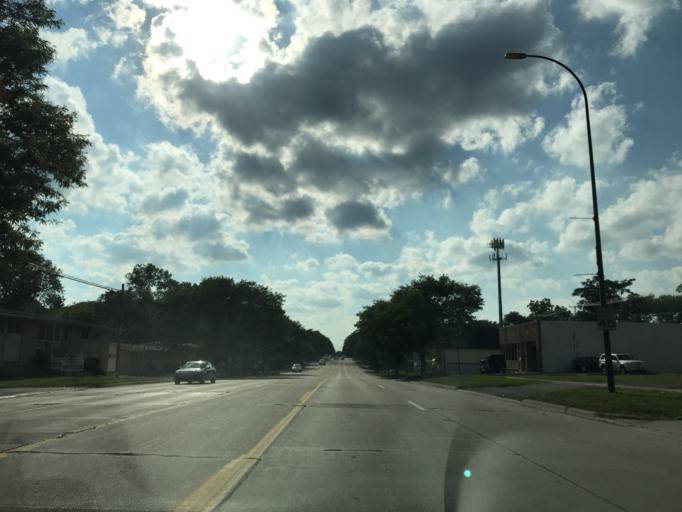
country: US
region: Michigan
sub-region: Wayne County
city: Redford
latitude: 42.3999
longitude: -83.2832
